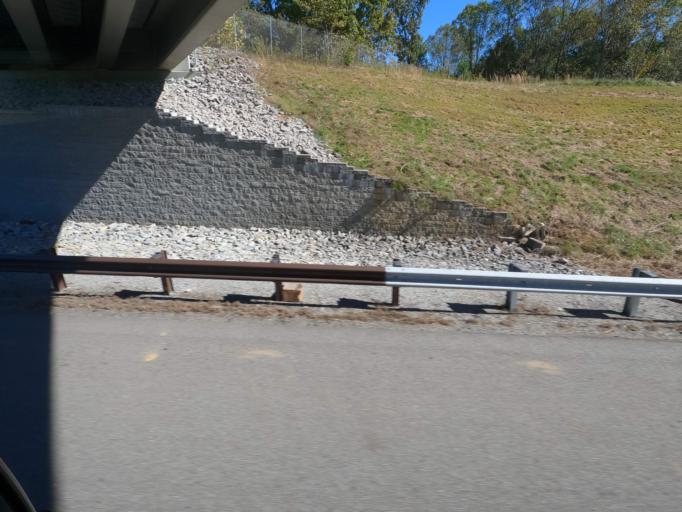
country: US
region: Tennessee
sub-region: Williamson County
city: Fairview
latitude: 35.8471
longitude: -87.0666
